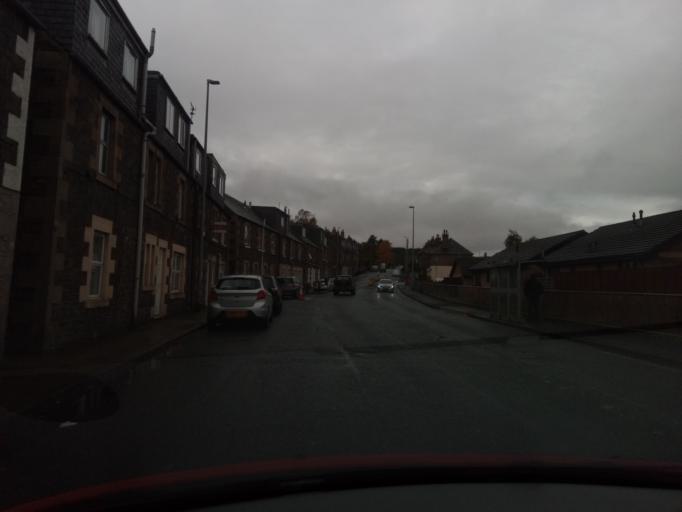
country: GB
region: Scotland
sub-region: The Scottish Borders
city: Galashiels
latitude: 55.6245
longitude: -2.8281
